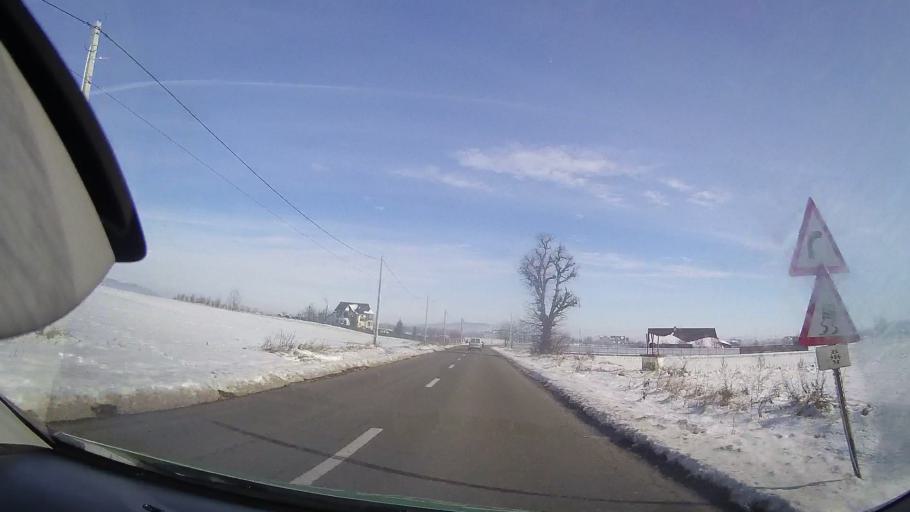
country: RO
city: Vanatori-Neamt
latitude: 47.1734
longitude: 26.3143
